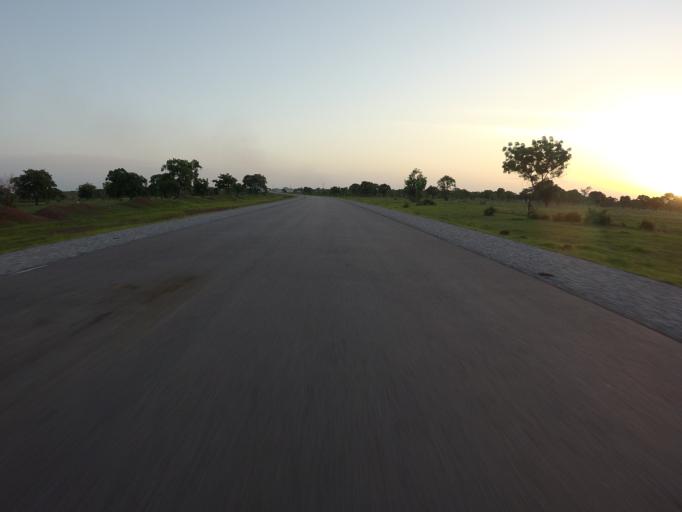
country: GH
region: Northern
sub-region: Yendi
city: Yendi
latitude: 9.9614
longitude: -0.1440
